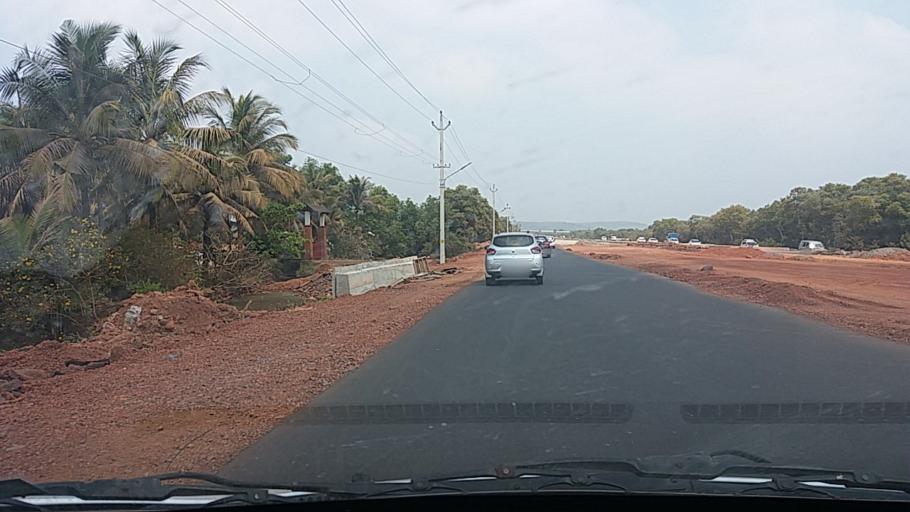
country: IN
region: Goa
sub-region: North Goa
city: Bambolim
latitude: 15.4813
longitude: 73.8476
